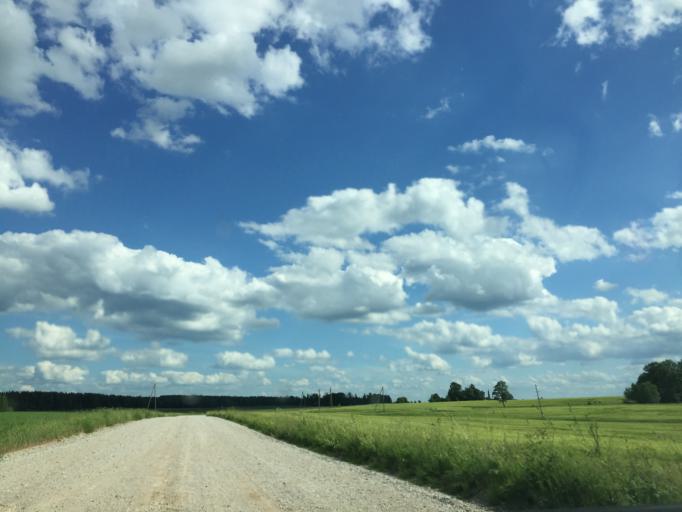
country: LV
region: Jaunpils
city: Jaunpils
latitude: 56.8332
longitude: 23.0542
